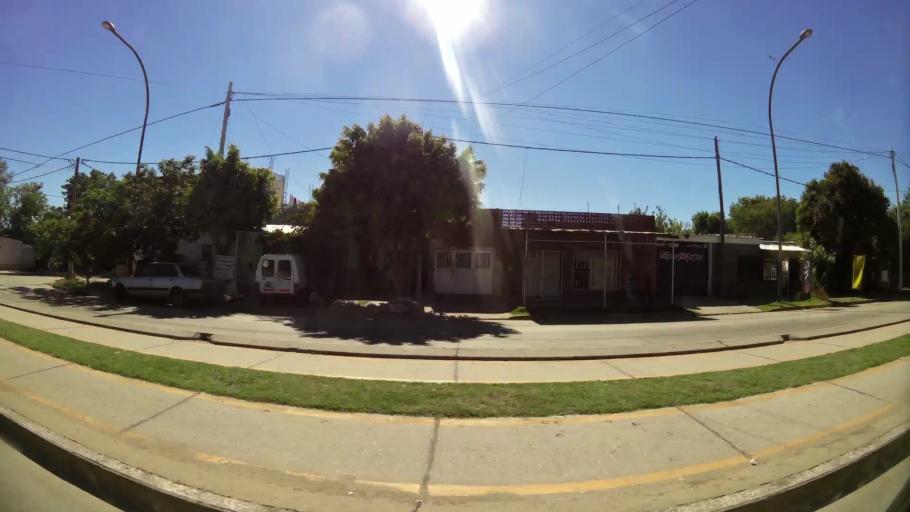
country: AR
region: Santa Fe
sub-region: Departamento de Rosario
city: Rosario
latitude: -32.9699
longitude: -60.7011
